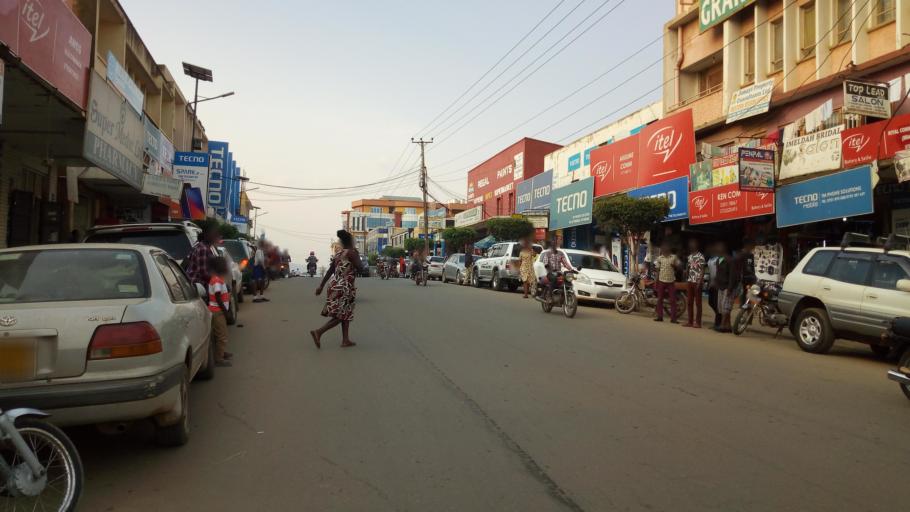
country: UG
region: Western Region
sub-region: Mbarara District
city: Mbarara
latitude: -0.6069
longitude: 30.6615
